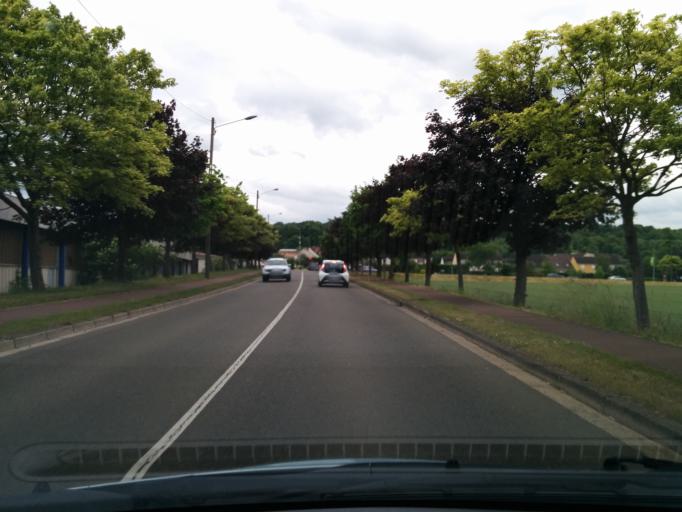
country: FR
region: Ile-de-France
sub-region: Departement des Yvelines
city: Aubergenville
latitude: 48.9631
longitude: 1.8514
